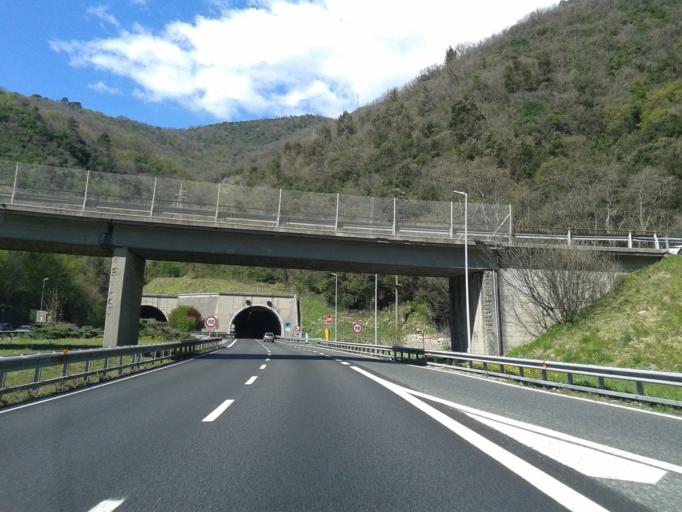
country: IT
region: Liguria
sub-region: Provincia di Genova
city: Recco
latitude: 44.3773
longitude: 9.1438
